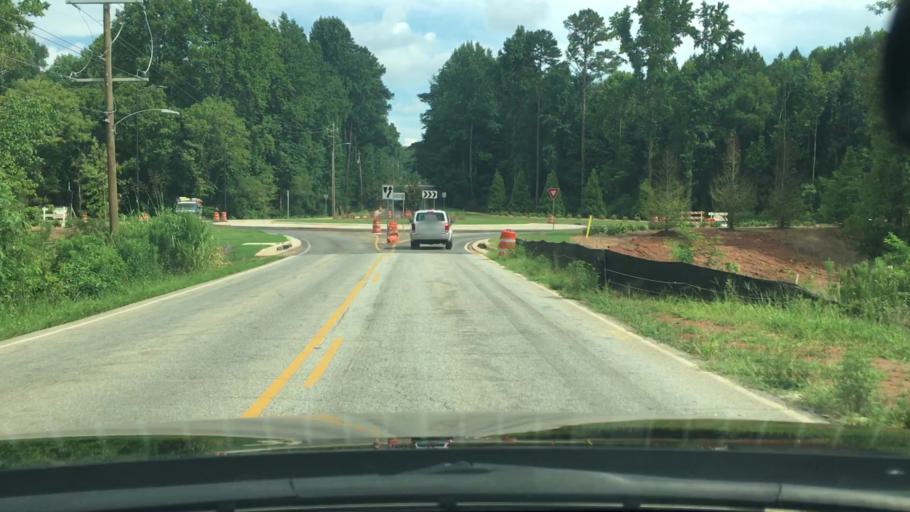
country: US
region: Georgia
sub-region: Coweta County
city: Newnan
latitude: 33.3779
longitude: -84.7806
